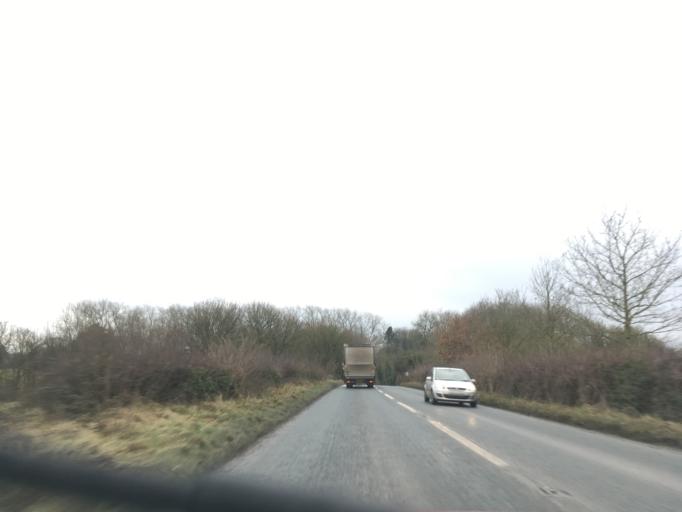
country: GB
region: England
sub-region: Gloucestershire
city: Tetbury
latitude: 51.6513
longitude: -2.1350
